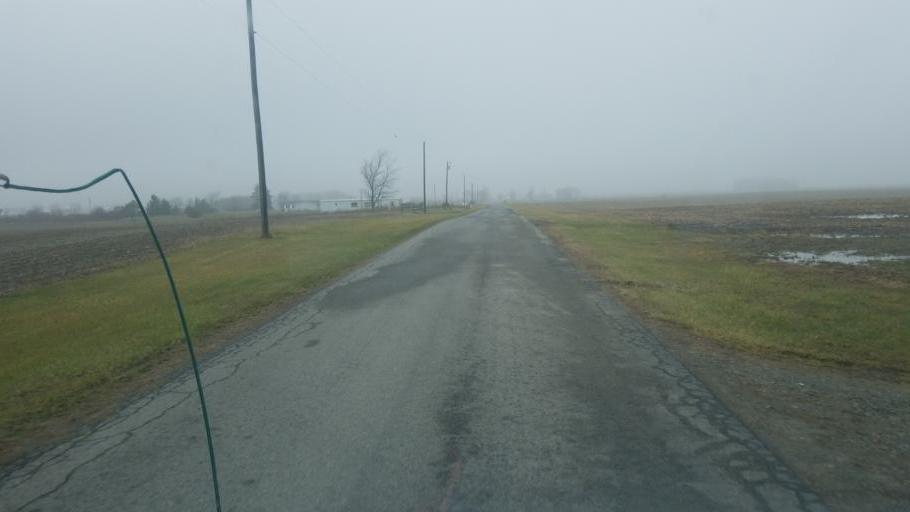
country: US
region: Ohio
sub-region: Champaign County
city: North Lewisburg
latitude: 40.3771
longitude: -83.5251
